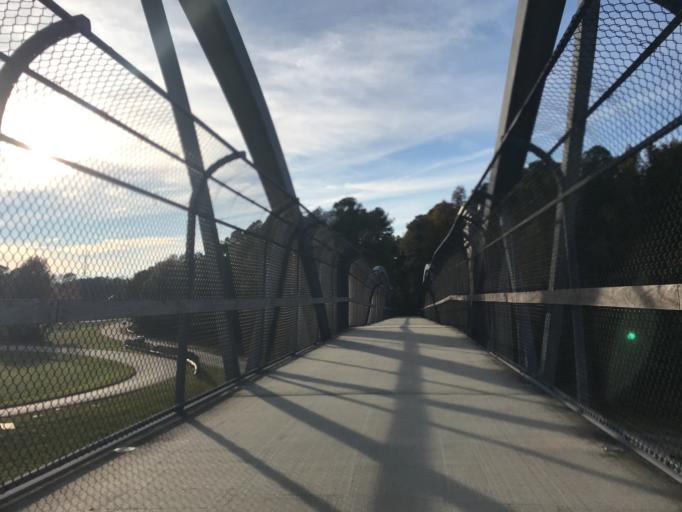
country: US
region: North Carolina
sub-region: Wake County
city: West Raleigh
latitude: 35.8056
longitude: -78.6939
